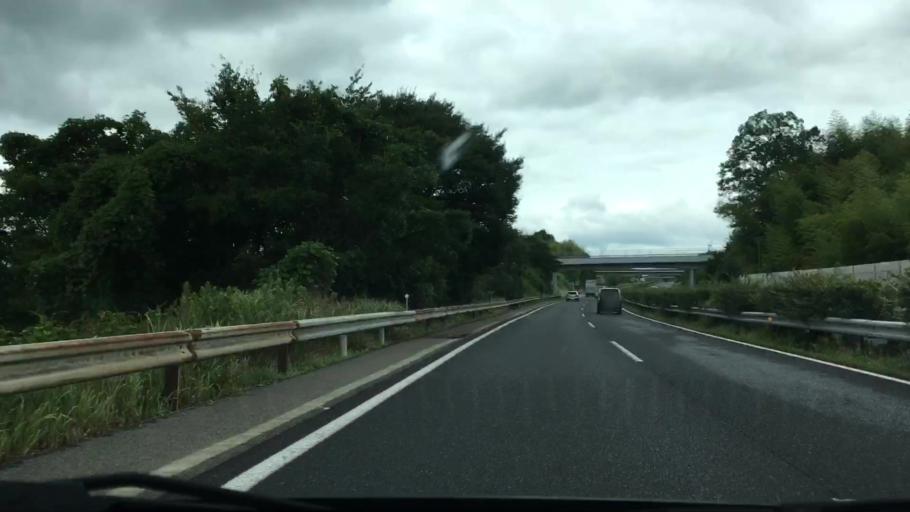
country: JP
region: Okayama
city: Tsuyama
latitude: 35.0637
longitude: 133.9801
